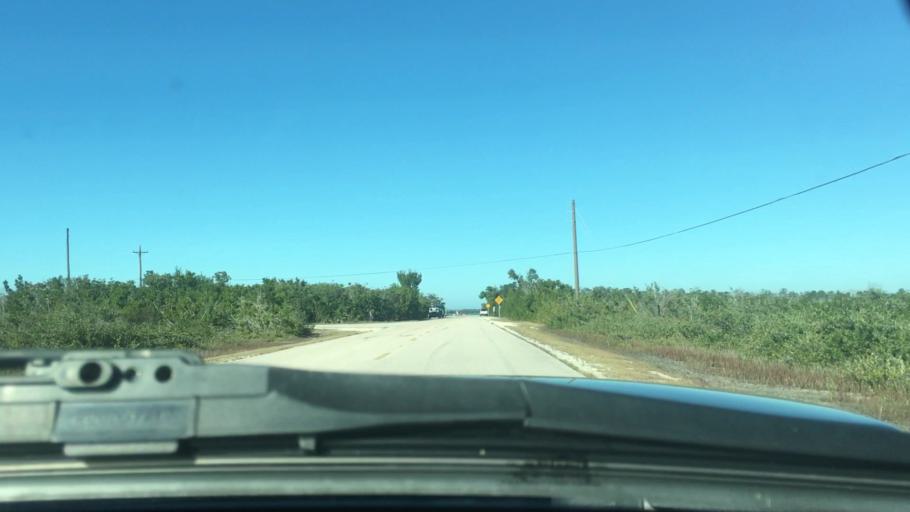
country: US
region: Florida
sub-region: Monroe County
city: Cudjoe Key
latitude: 24.6926
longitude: -81.4996
